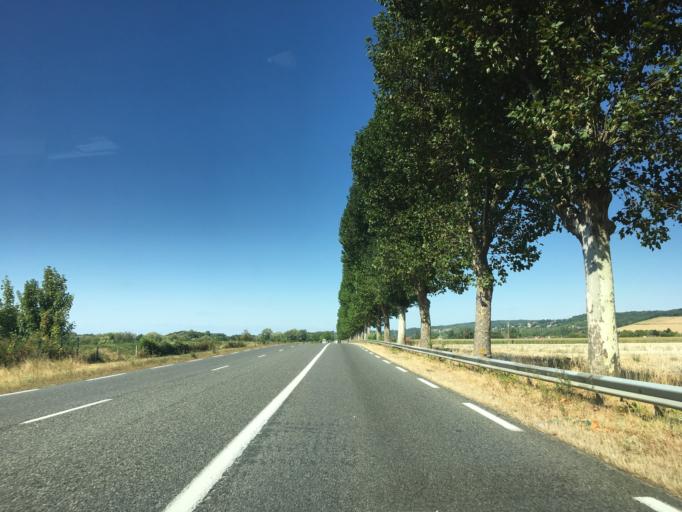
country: FR
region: Bourgogne
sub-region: Departement de l'Yonne
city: Veron
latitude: 48.1241
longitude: 3.2940
